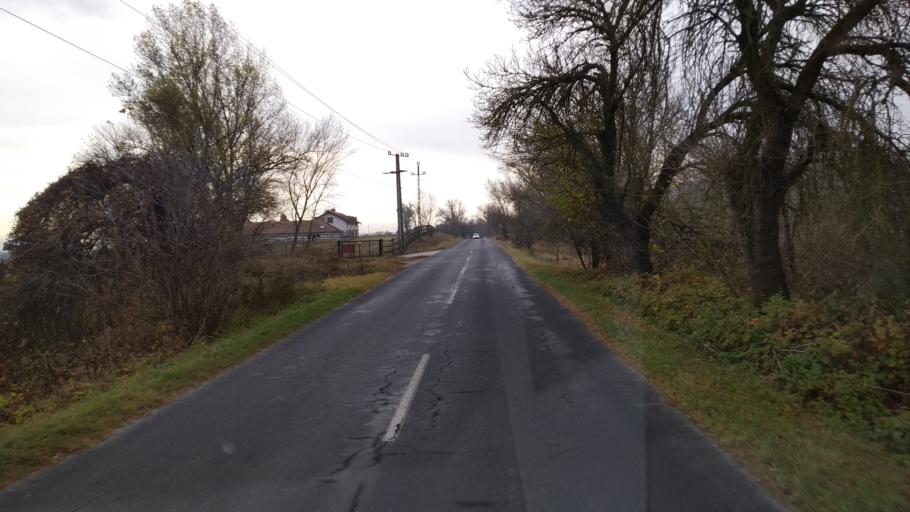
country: HU
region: Pest
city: Tahitotfalu
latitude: 47.7799
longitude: 19.0927
